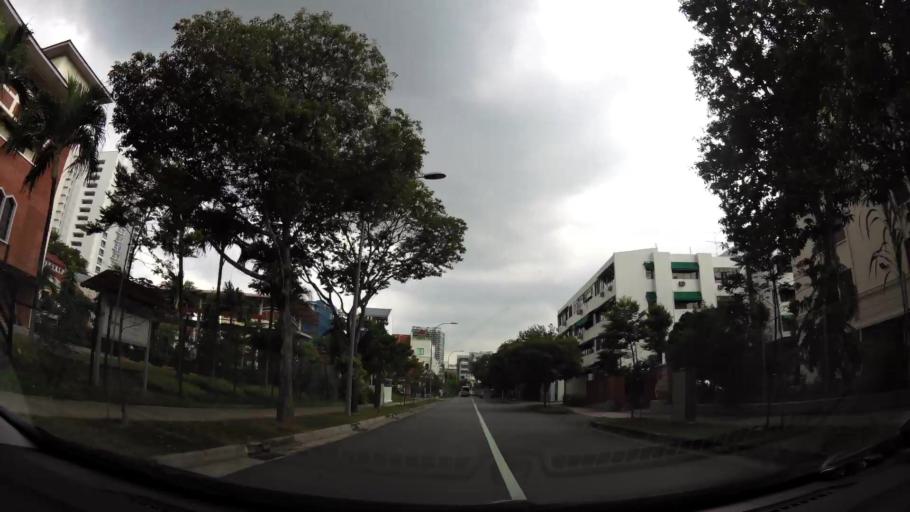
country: SG
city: Singapore
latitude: 1.3132
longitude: 103.8467
